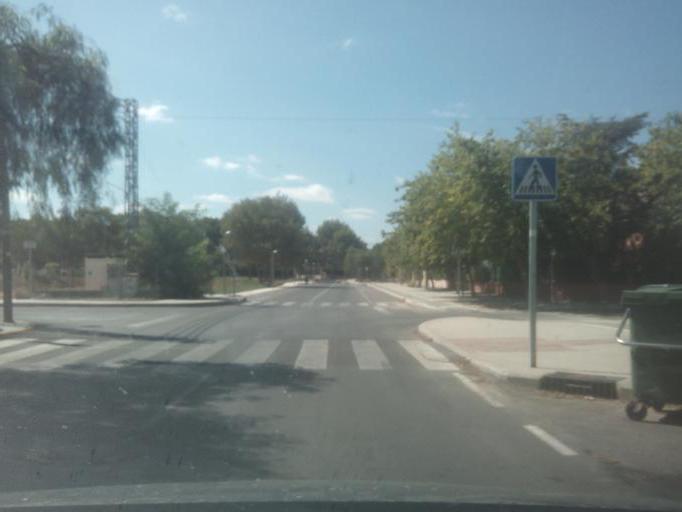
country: ES
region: Valencia
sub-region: Provincia de Valencia
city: Manises
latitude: 39.5347
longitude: -0.4905
